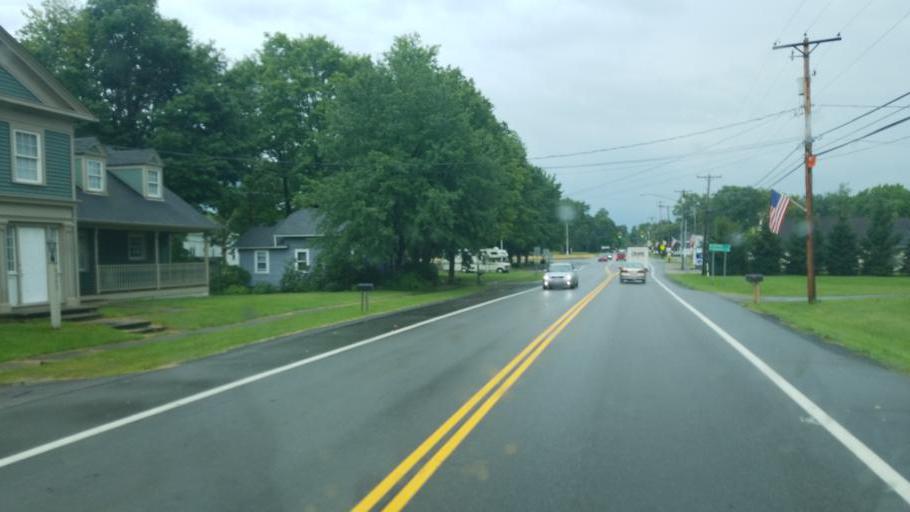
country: US
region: Ohio
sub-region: Trumbull County
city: Champion Heights
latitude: 41.3890
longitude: -80.8692
